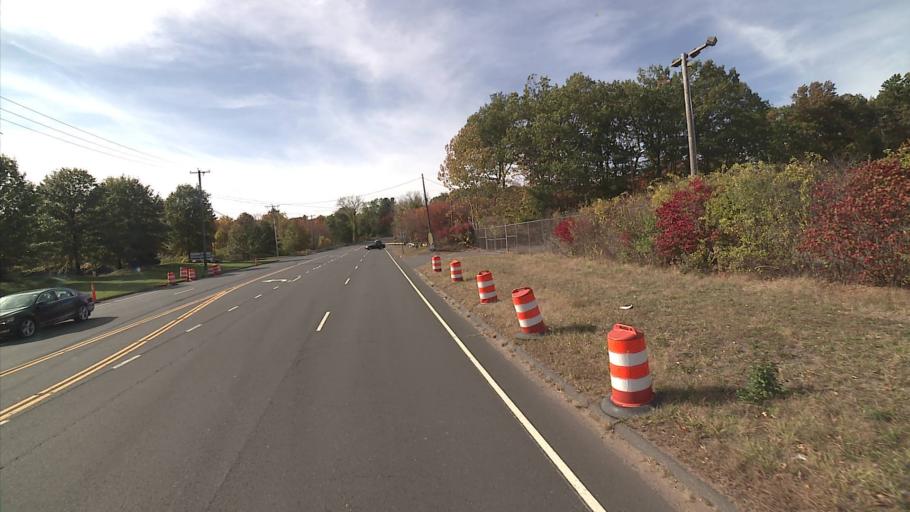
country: US
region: Connecticut
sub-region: Hartford County
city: Plainville
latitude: 41.7046
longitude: -72.8635
